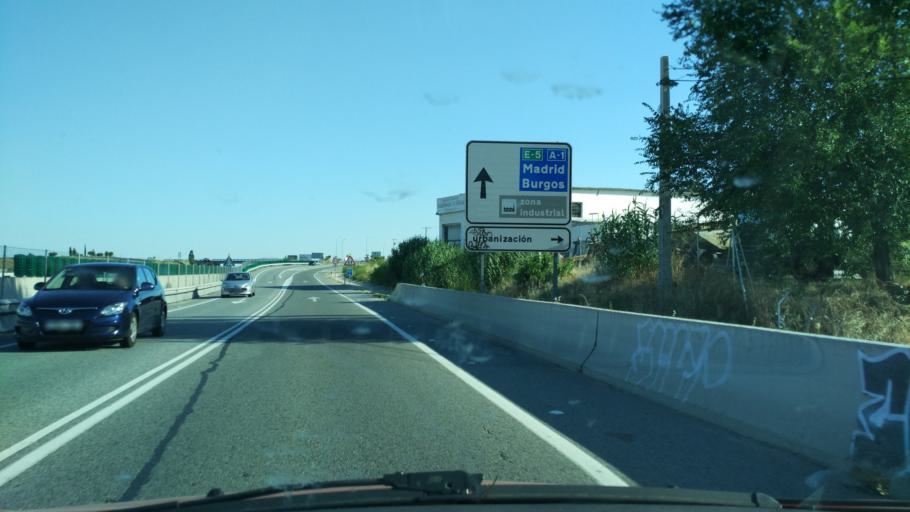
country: ES
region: Madrid
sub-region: Provincia de Madrid
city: El Molar
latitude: 40.7205
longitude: -3.5780
